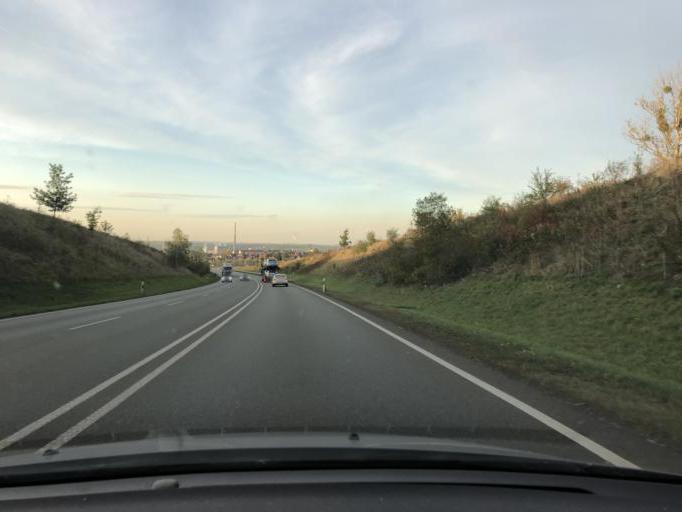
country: DE
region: Saxony-Anhalt
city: Zeitz
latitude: 51.0301
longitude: 12.1262
